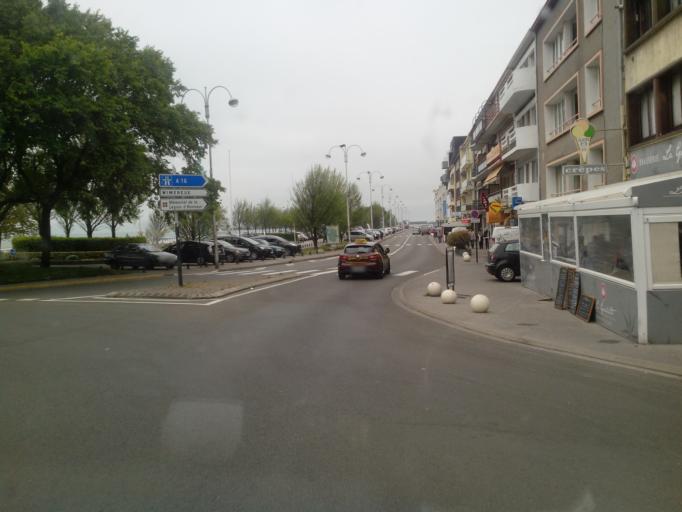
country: FR
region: Nord-Pas-de-Calais
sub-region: Departement du Pas-de-Calais
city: Saint-Martin-Boulogne
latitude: 50.7314
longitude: 1.5956
